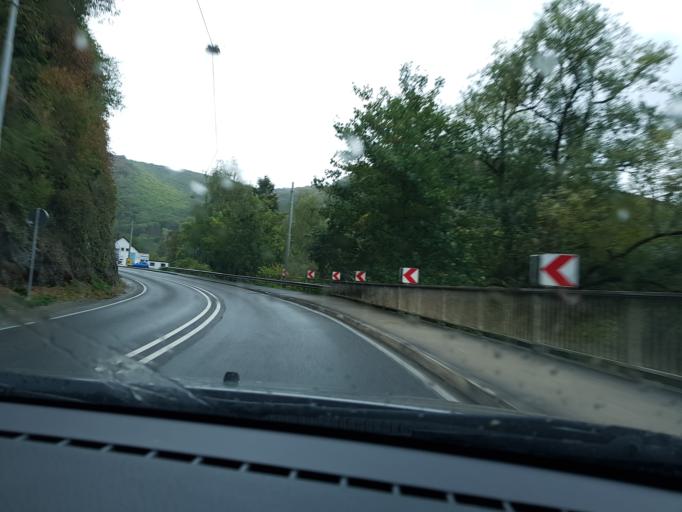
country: DE
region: Rheinland-Pfalz
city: Bad Ems
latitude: 50.3197
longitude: 7.7319
